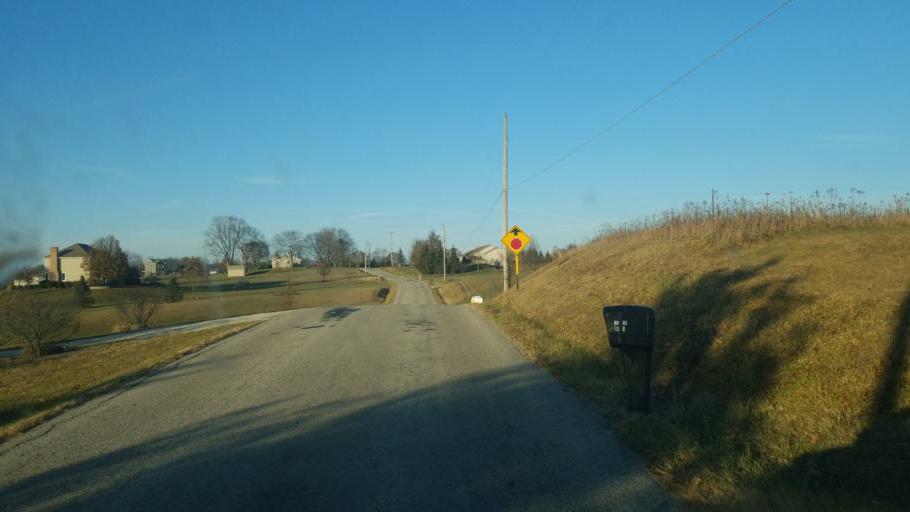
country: US
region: Ohio
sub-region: Richland County
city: Ontario
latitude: 40.7348
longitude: -82.6567
